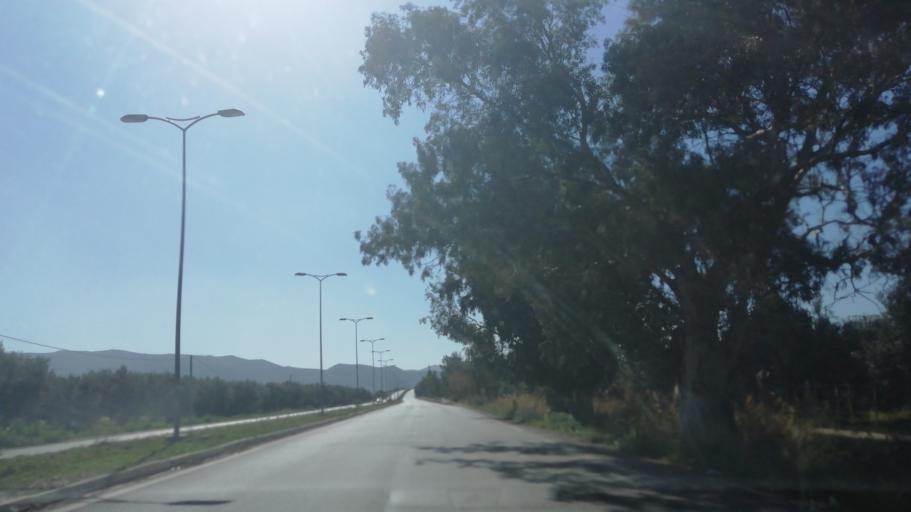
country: DZ
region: Mascara
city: Sig
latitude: 35.5450
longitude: -0.2052
